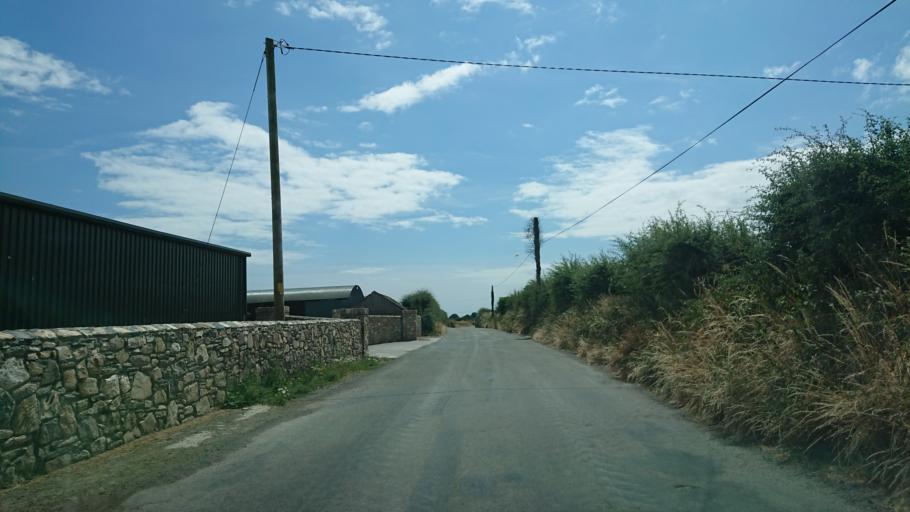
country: IE
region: Munster
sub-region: Waterford
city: Portlaw
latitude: 52.1852
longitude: -7.3325
